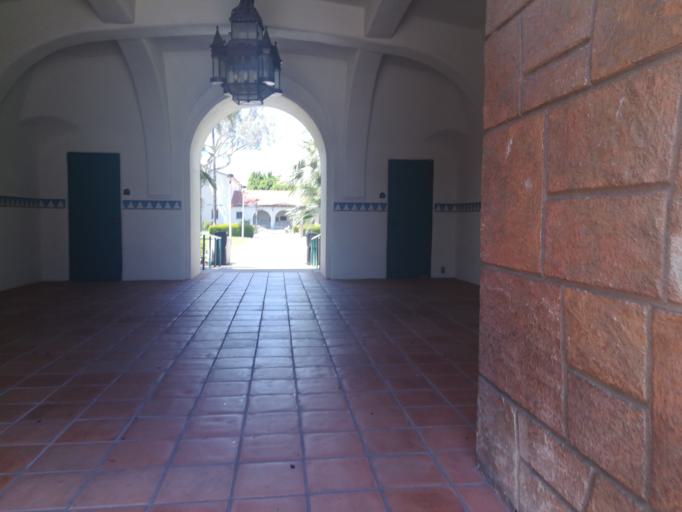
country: US
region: California
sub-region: San Diego County
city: La Mesa
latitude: 32.7764
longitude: -117.0719
